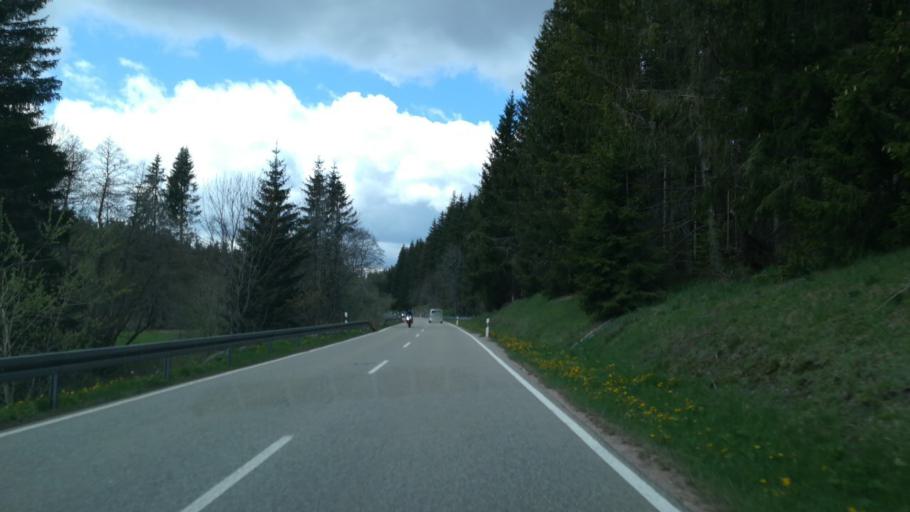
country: DE
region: Baden-Wuerttemberg
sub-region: Freiburg Region
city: Schluchsee
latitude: 47.7977
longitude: 8.2112
